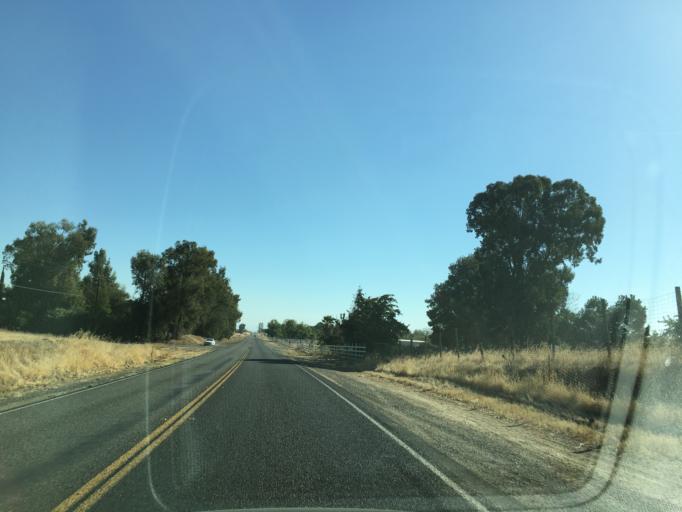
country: US
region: California
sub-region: Madera County
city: Parksdale
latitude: 36.9960
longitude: -119.9890
